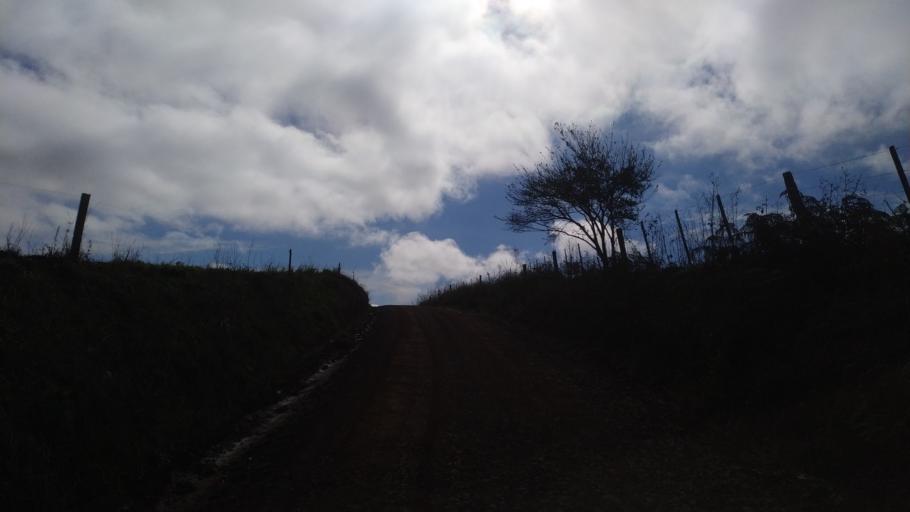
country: BR
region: Santa Catarina
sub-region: Chapeco
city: Chapeco
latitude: -27.1541
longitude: -52.5952
